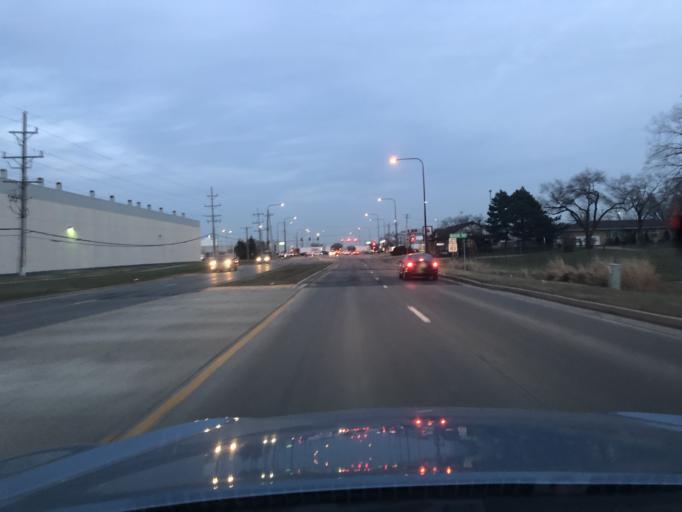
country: US
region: Illinois
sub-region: Cook County
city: Elk Grove Village
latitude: 41.9930
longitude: -87.9627
